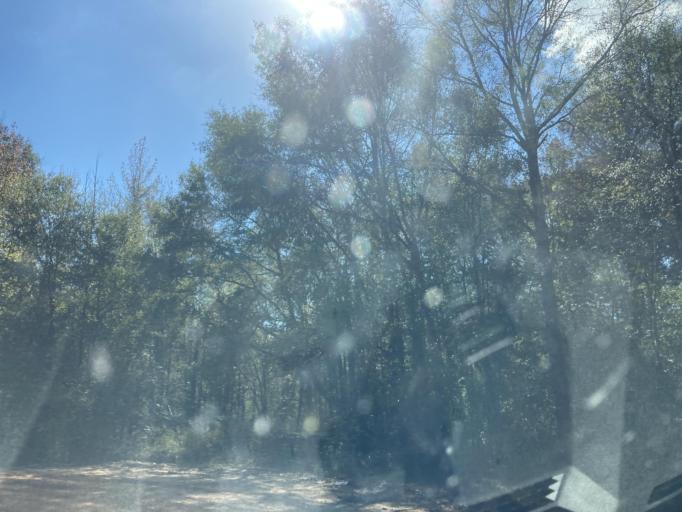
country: US
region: Mississippi
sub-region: Lamar County
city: Sumrall
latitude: 31.3128
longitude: -89.5419
